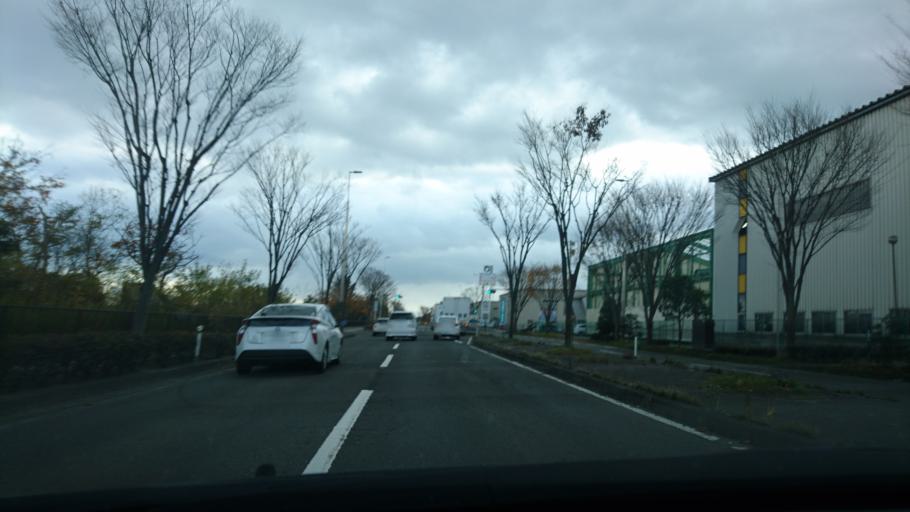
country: JP
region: Miyagi
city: Iwanuma
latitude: 38.1339
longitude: 140.9115
